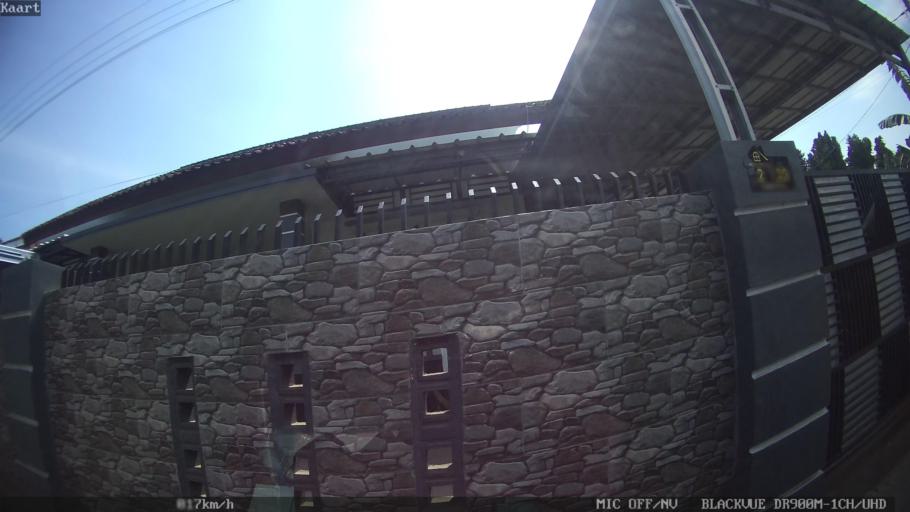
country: ID
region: Lampung
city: Kedaton
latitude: -5.3892
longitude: 105.2441
